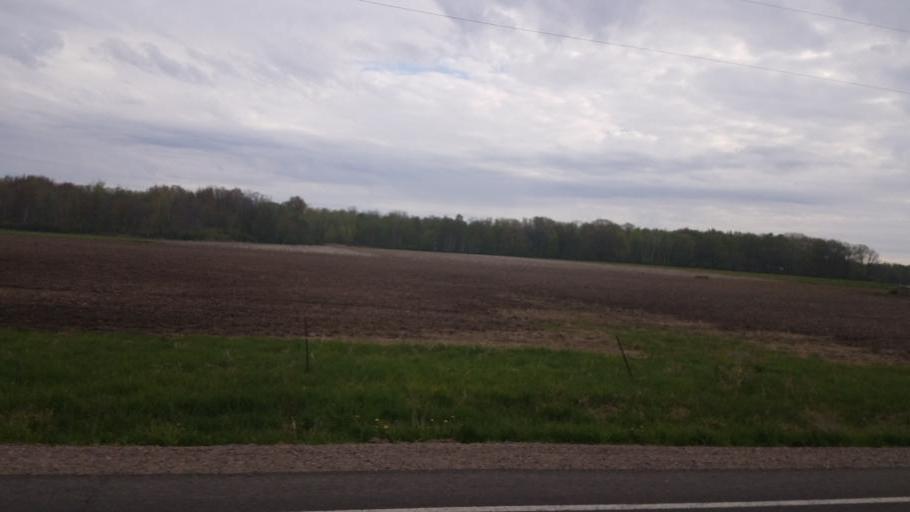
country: US
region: Wisconsin
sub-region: Marathon County
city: Spencer
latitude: 44.6557
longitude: -90.3620
